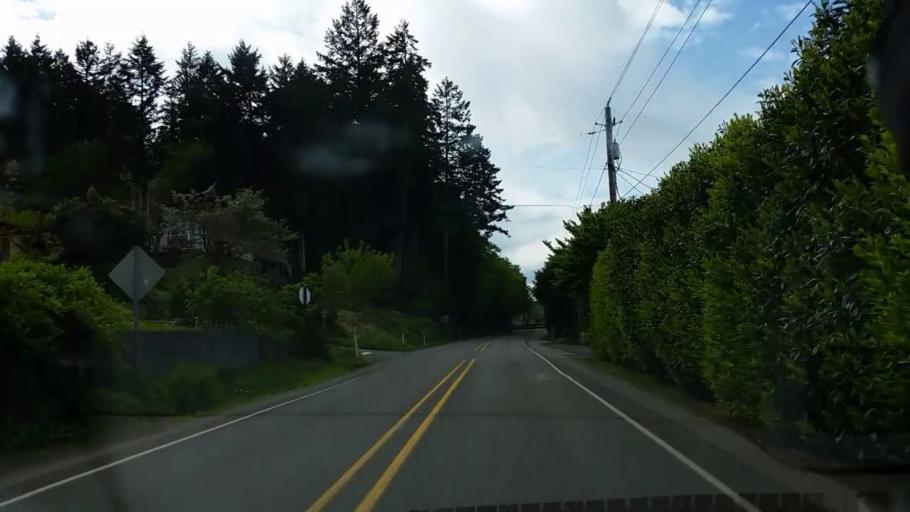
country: US
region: Washington
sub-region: Mason County
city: Shelton
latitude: 47.3573
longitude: -123.1015
